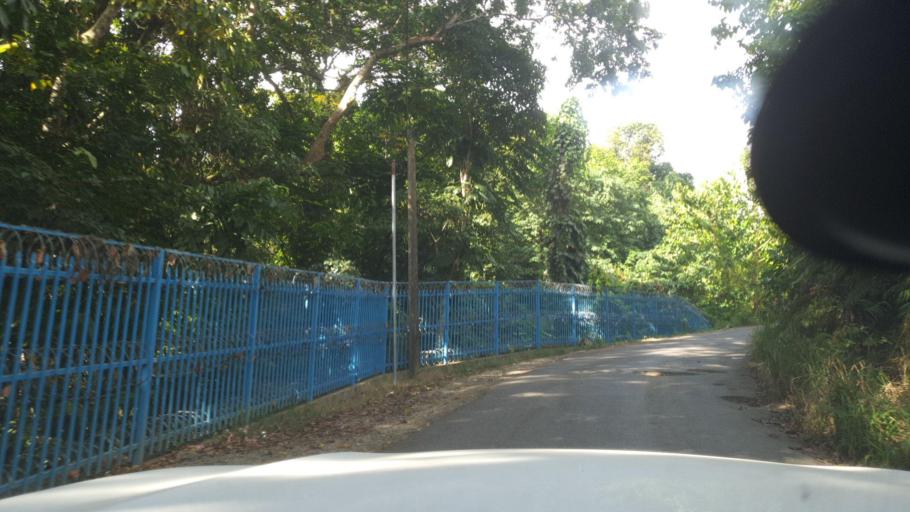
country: SB
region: Guadalcanal
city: Honiara
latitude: -9.4365
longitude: 159.9409
